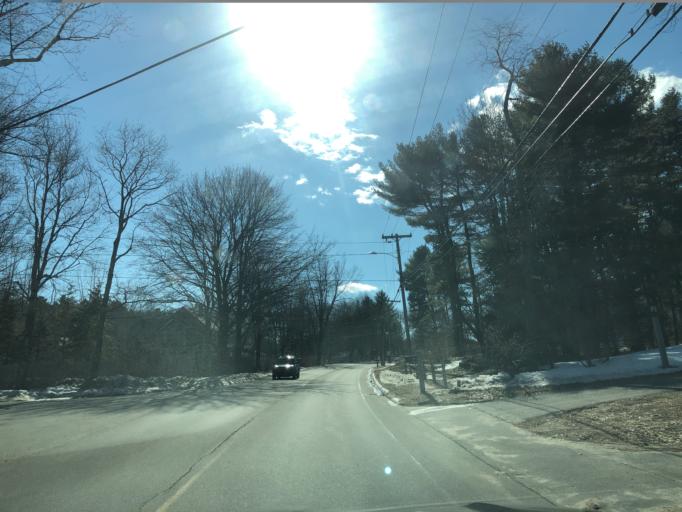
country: US
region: Maine
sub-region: Cumberland County
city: Falmouth
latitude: 43.7146
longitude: -70.2663
